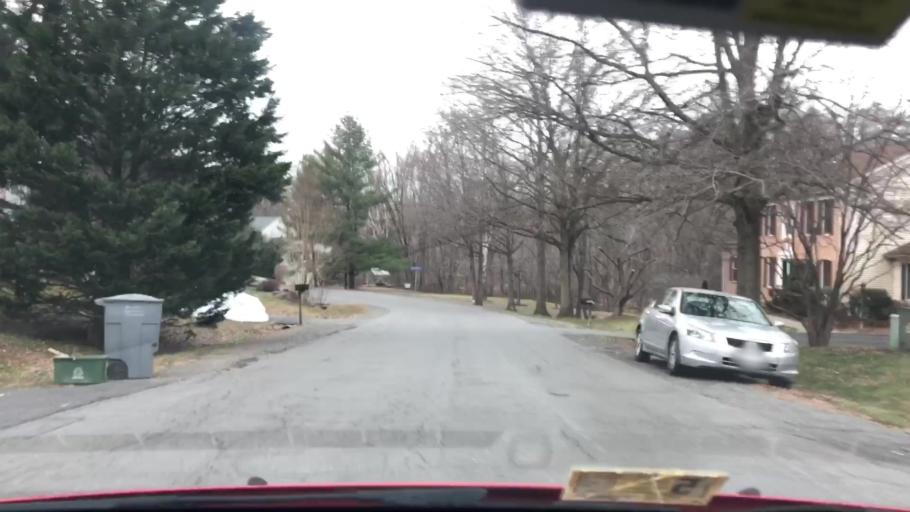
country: US
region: Virginia
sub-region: Fairfax County
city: Wolf Trap
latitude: 38.9644
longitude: -77.2809
